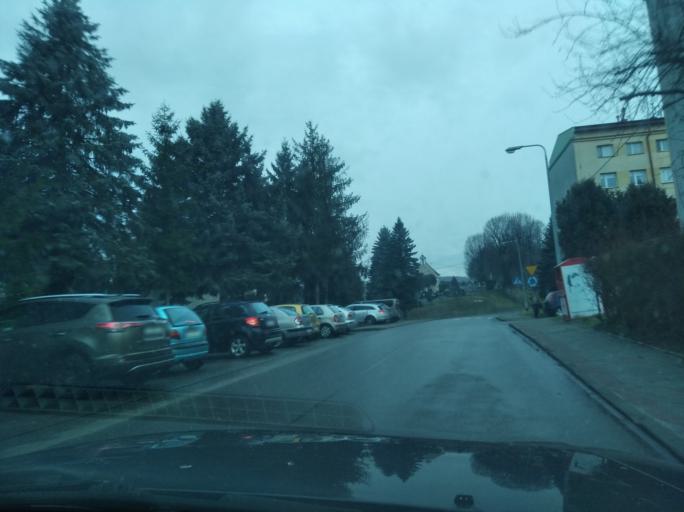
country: PL
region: Subcarpathian Voivodeship
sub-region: Powiat strzyzowski
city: Strzyzow
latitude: 49.8702
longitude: 21.7844
